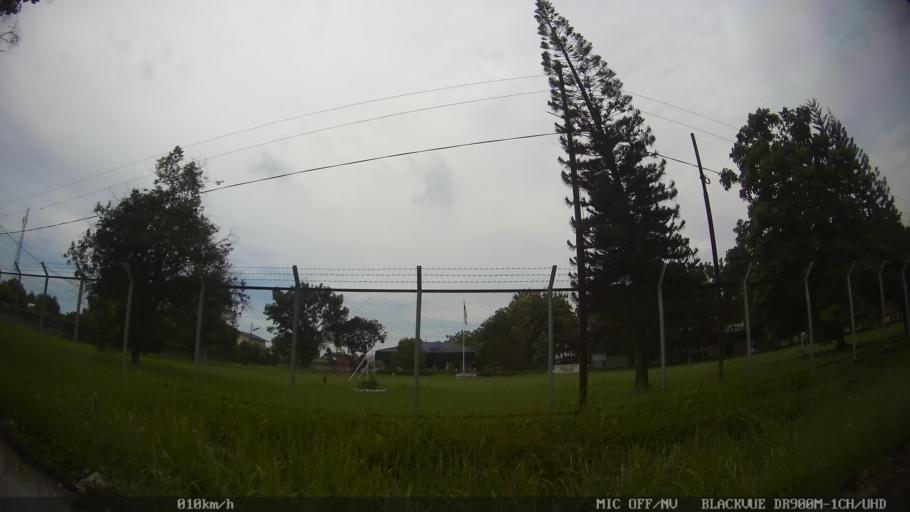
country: ID
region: North Sumatra
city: Sunggal
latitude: 3.6191
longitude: 98.5804
